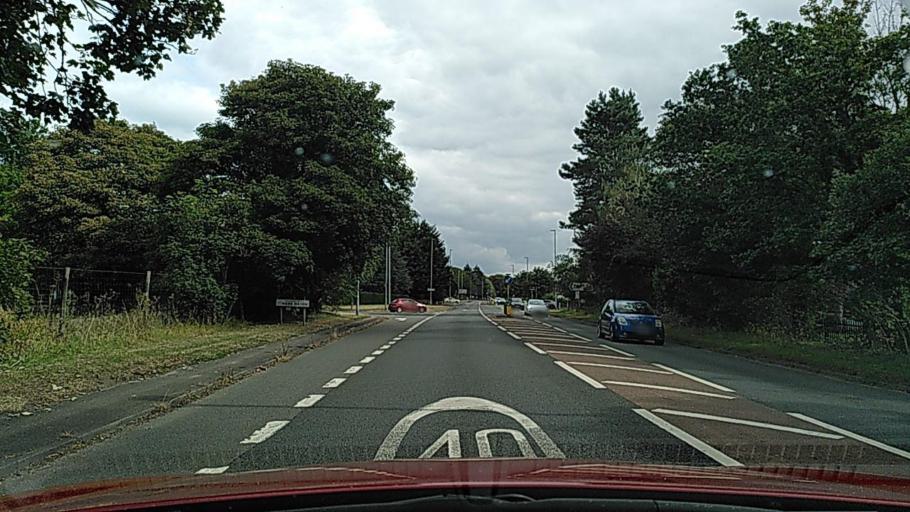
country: GB
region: England
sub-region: Wokingham
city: Wargrave
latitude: 51.4940
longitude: -0.8511
